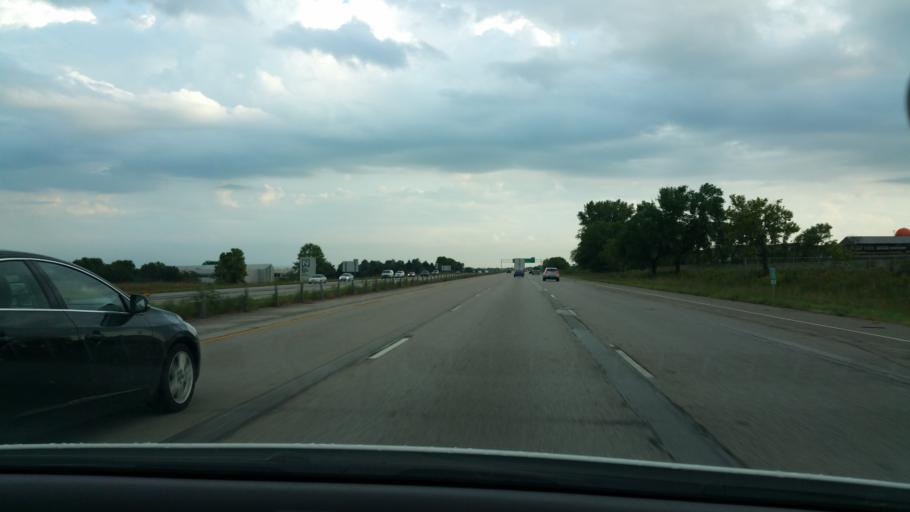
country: US
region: Iowa
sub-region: Polk County
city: Ankeny
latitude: 41.6978
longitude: -93.5762
